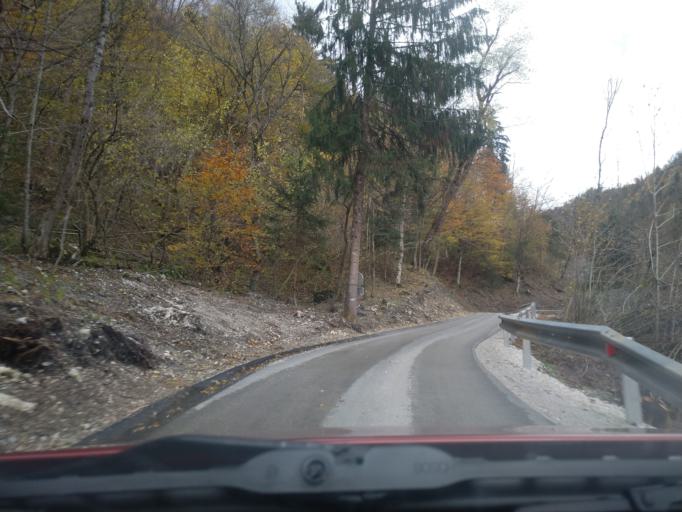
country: SI
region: Kamnik
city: Mekinje
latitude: 46.2628
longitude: 14.6412
